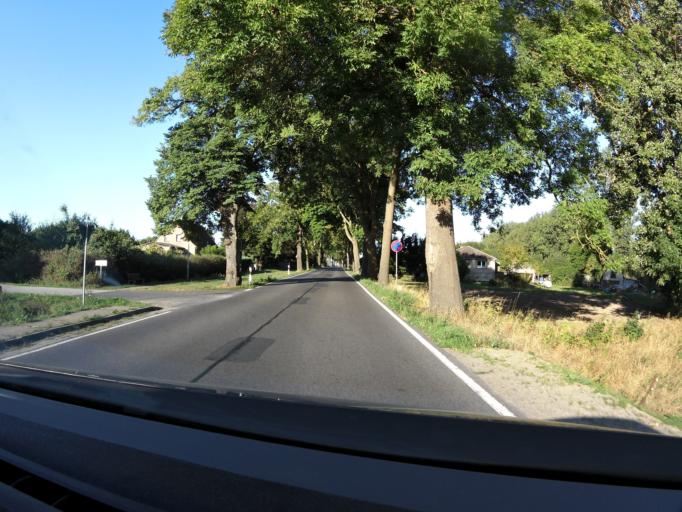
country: DE
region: Mecklenburg-Vorpommern
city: Anklam
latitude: 53.8508
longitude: 13.6342
